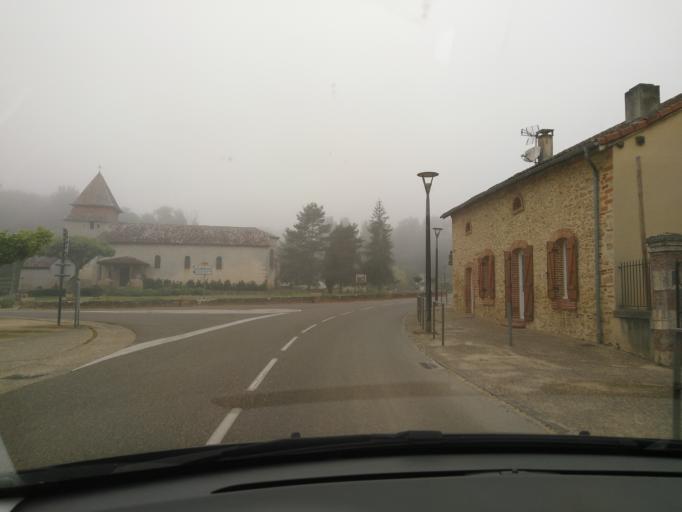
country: FR
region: Aquitaine
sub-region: Departement des Landes
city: Villeneuve-de-Marsan
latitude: 43.8896
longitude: -0.3913
